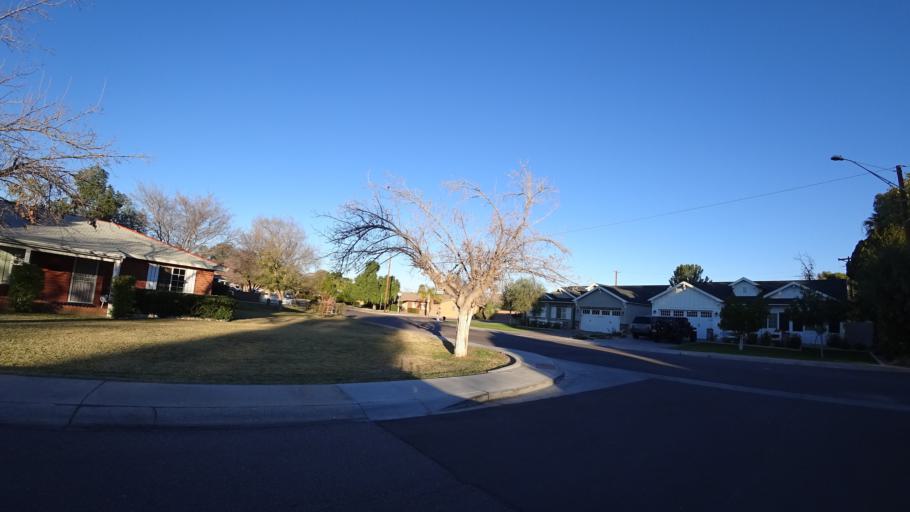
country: US
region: Arizona
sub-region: Maricopa County
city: Paradise Valley
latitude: 33.4917
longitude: -112.0020
